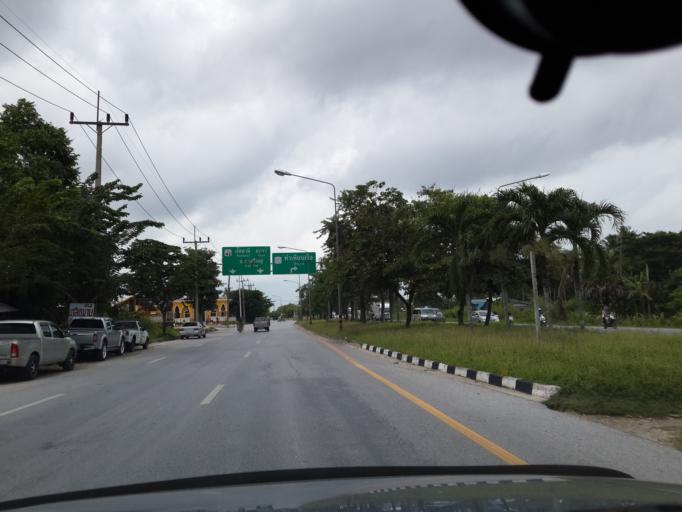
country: TH
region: Pattani
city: Pattani
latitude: 6.8707
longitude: 101.2843
